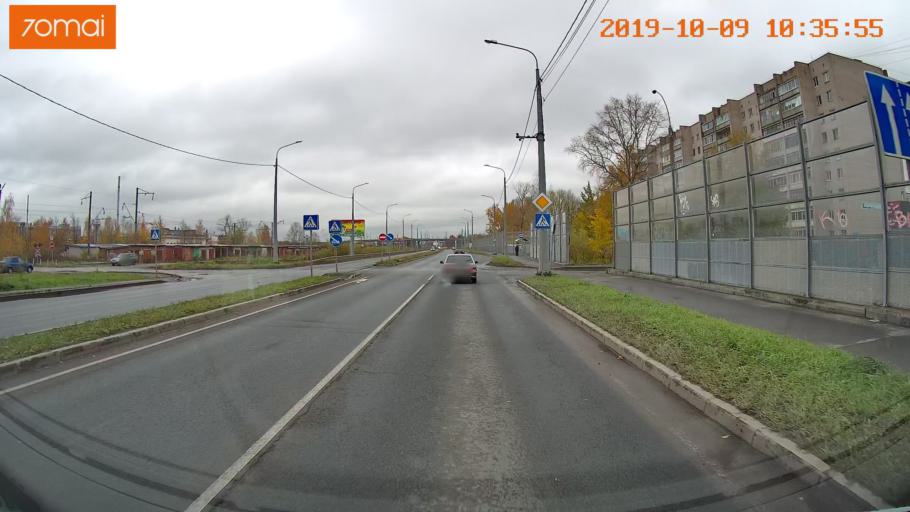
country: RU
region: Vologda
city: Vologda
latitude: 59.2291
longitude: 39.8624
